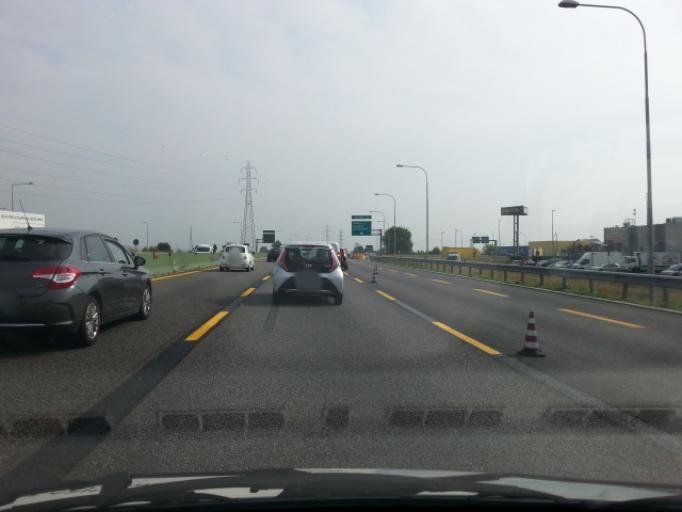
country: IT
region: Piedmont
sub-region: Provincia di Torino
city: Collegno
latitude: 45.0973
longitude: 7.5748
